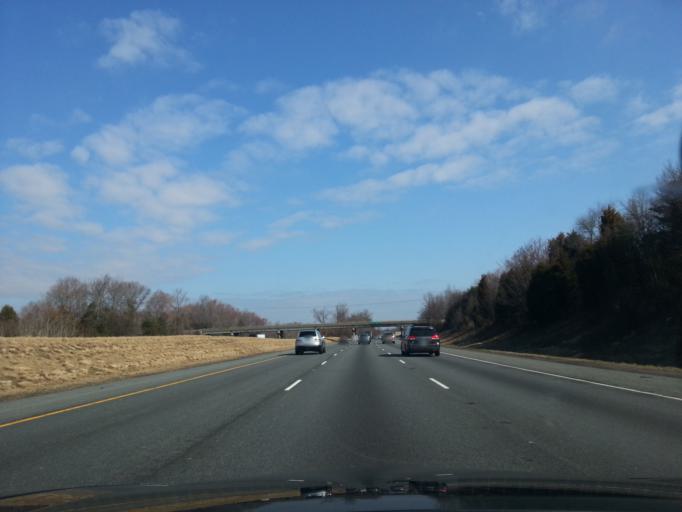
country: US
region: Virginia
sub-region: City of Fredericksburg
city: Fredericksburg
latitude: 38.2665
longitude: -77.5144
